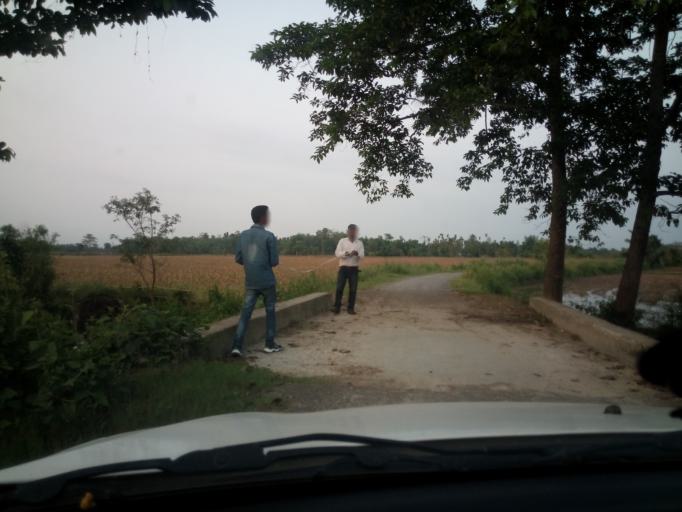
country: IN
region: Assam
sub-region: Udalguri
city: Udalguri
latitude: 26.6841
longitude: 92.1132
